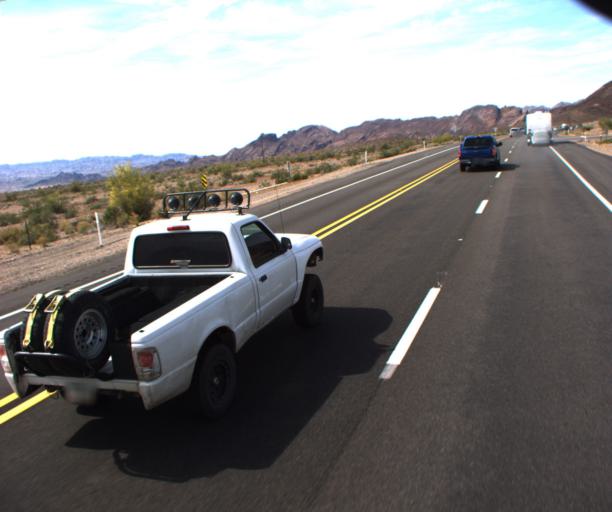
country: US
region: Arizona
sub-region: Mohave County
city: Desert Hills
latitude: 34.5840
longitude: -114.3685
